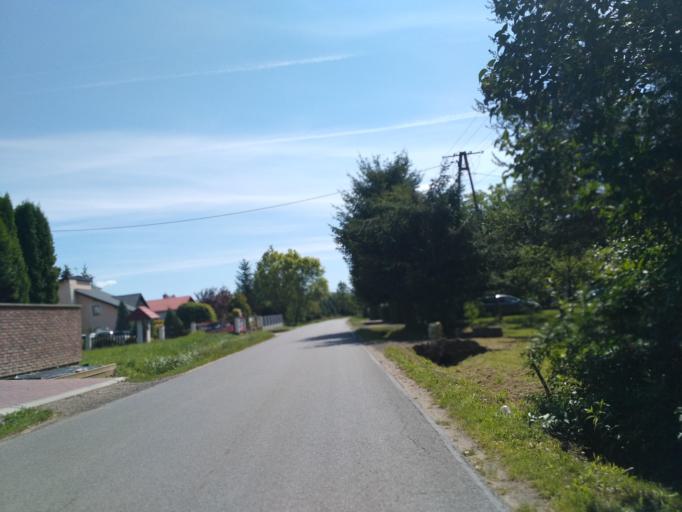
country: PL
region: Subcarpathian Voivodeship
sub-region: Powiat brzozowski
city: Jablonica Polska
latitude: 49.7002
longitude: 21.8771
